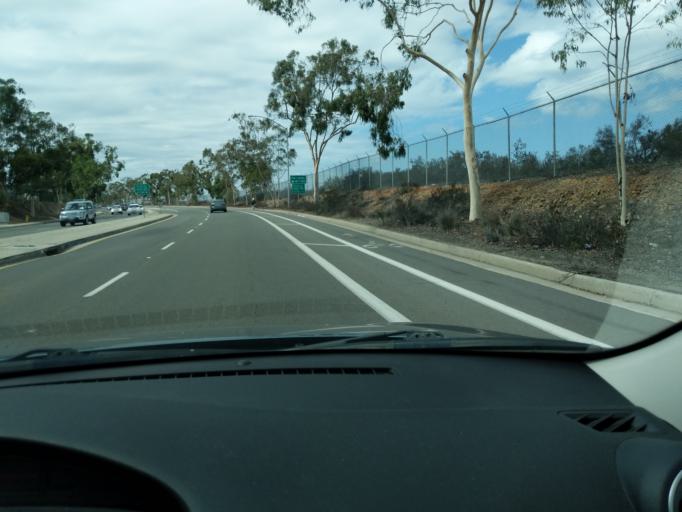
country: US
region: California
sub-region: San Diego County
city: San Diego
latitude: 32.8095
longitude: -117.1259
